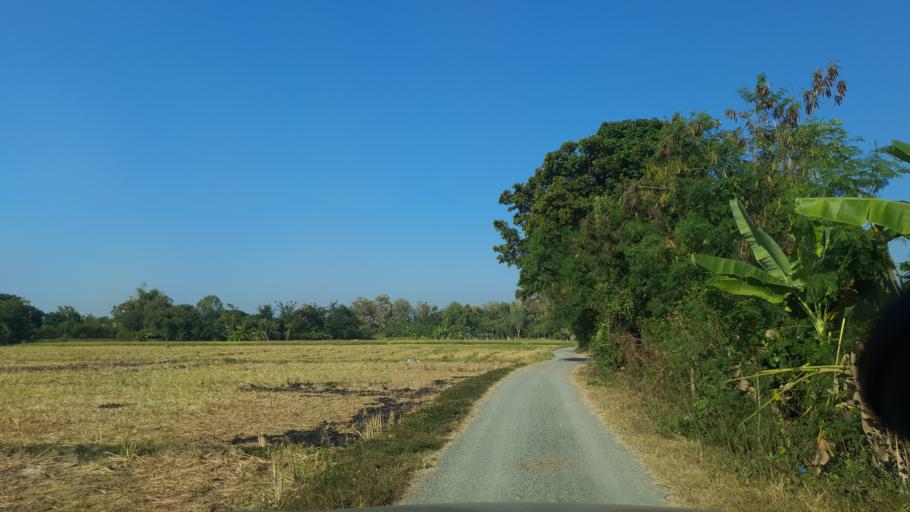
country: TH
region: Chiang Mai
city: San Kamphaeng
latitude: 18.7345
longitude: 99.1686
